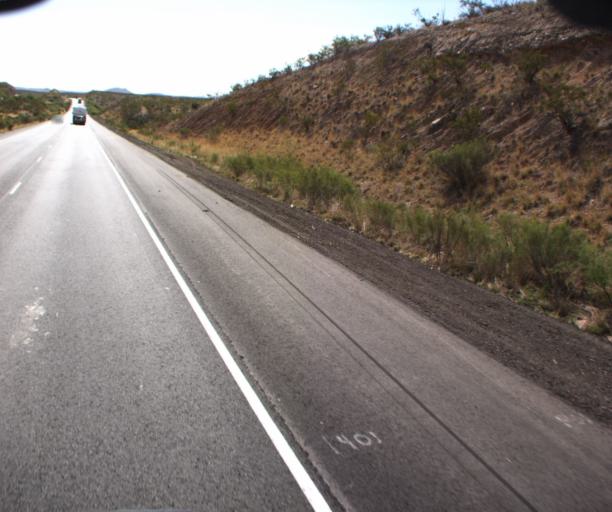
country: US
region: Arizona
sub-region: Pima County
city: Vail
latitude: 31.9908
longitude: -110.5998
